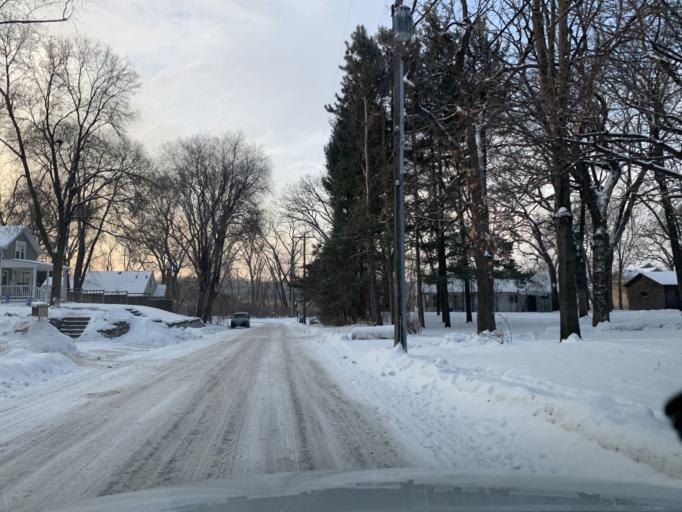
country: US
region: Minnesota
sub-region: Hennepin County
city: Saint Louis Park
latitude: 44.9249
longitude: -93.3593
